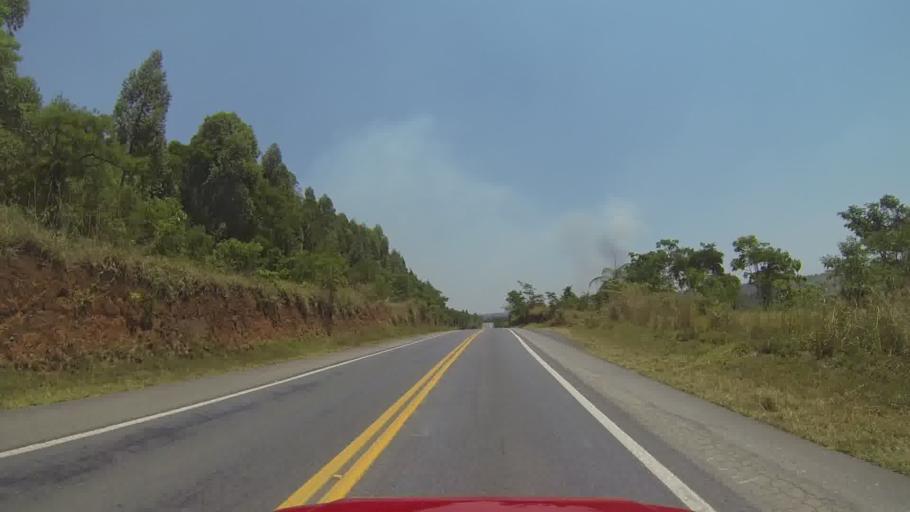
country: BR
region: Minas Gerais
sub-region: Itapecerica
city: Itapecerica
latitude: -20.3432
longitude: -45.2554
